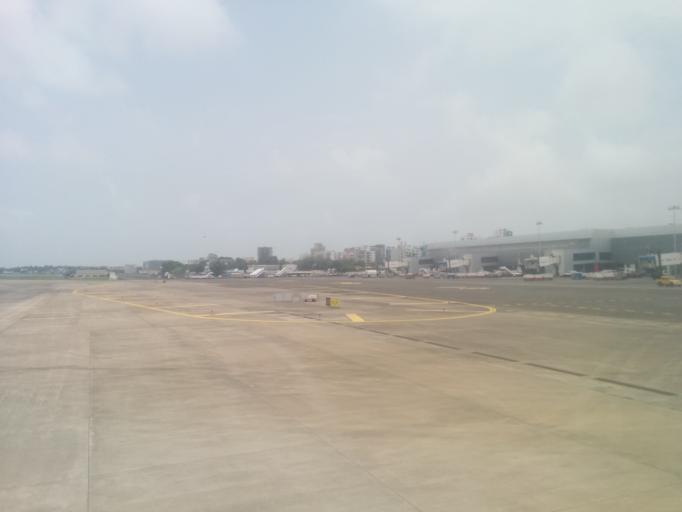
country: IN
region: Maharashtra
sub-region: Mumbai Suburban
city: Mumbai
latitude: 19.0903
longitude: 72.8540
